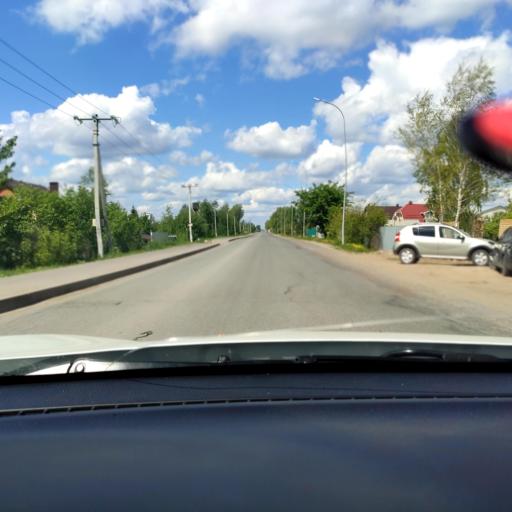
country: RU
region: Tatarstan
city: Stolbishchi
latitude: 55.6973
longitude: 49.1905
